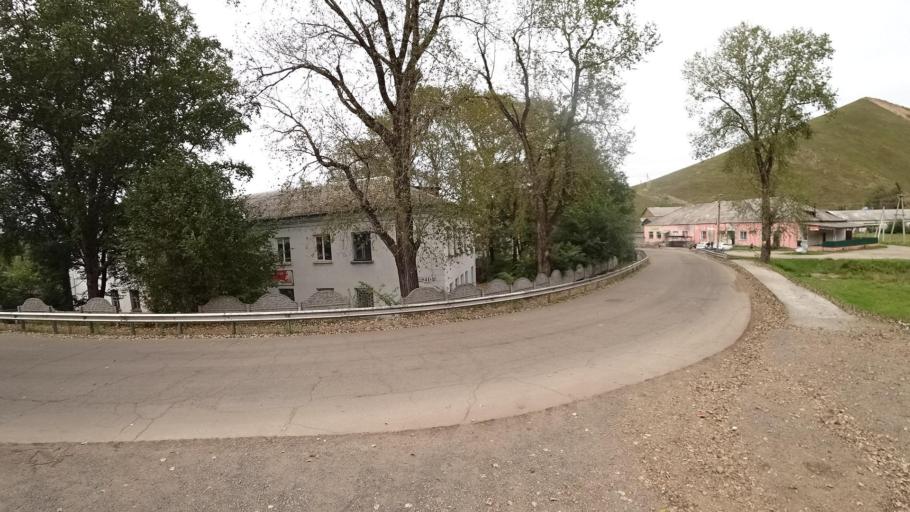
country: RU
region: Jewish Autonomous Oblast
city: Khingansk
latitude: 49.0188
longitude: 131.0631
